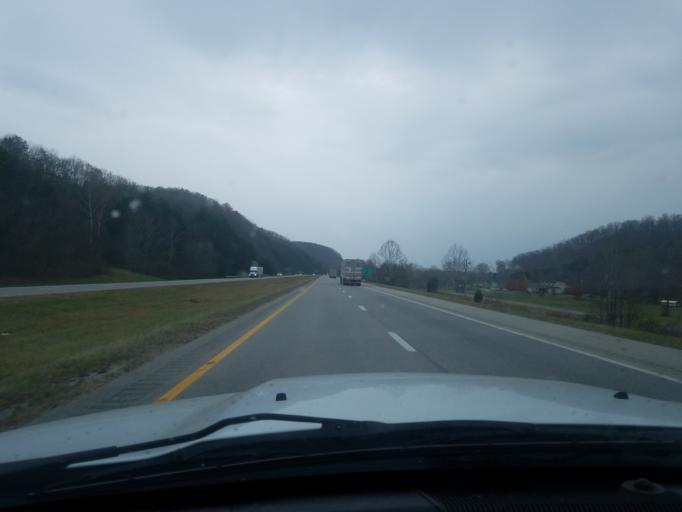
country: US
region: Kentucky
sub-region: Rowan County
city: Morehead
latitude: 38.1753
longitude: -83.5760
